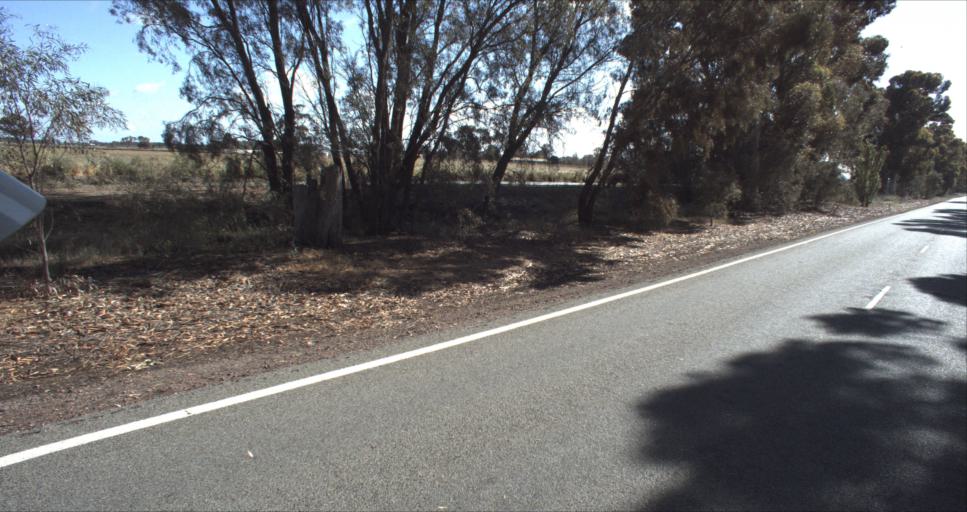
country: AU
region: New South Wales
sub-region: Leeton
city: Leeton
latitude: -34.5468
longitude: 146.3251
